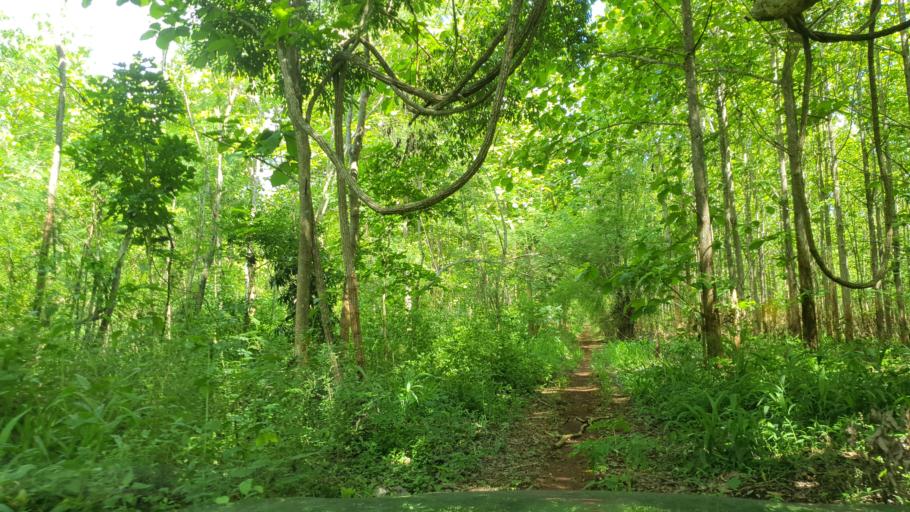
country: TH
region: Chiang Mai
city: Mae Taeng
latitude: 19.0782
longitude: 99.0961
